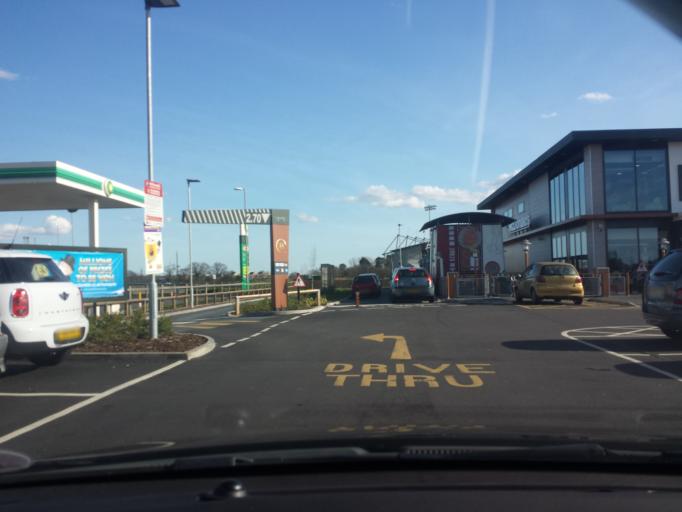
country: GB
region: England
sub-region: Essex
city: Great Horkesley
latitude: 51.9255
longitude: 0.8975
